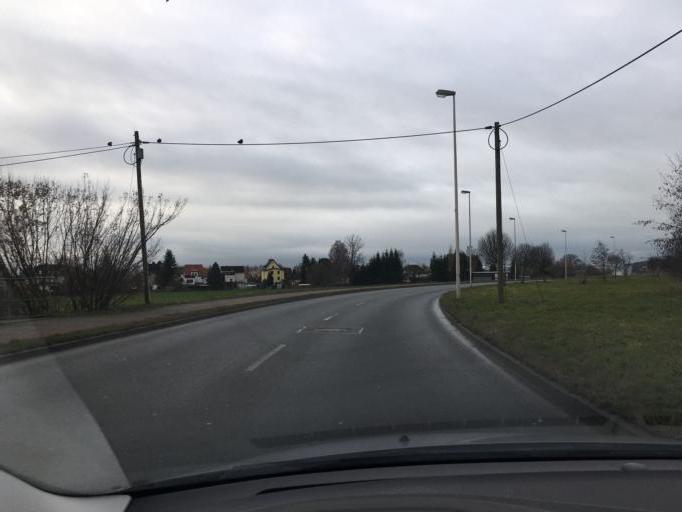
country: DE
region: Saxony
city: Glauchau
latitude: 50.8394
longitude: 12.5373
